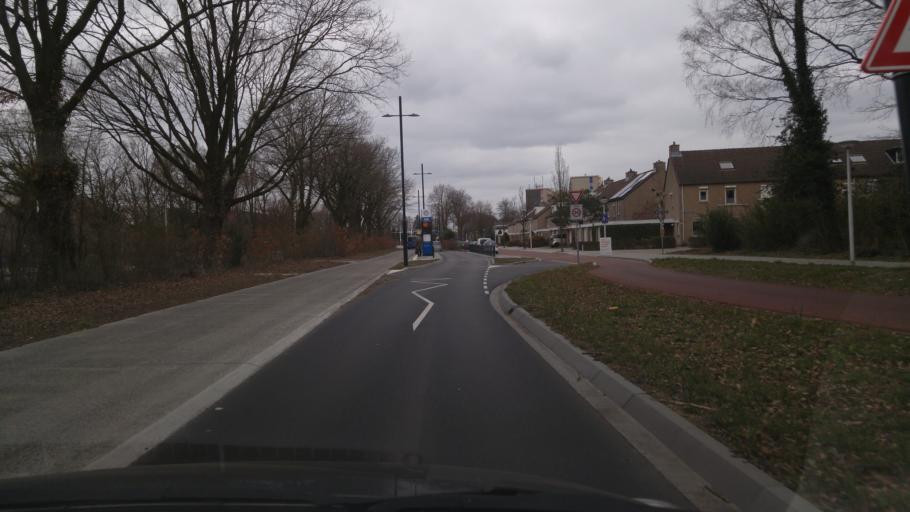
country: NL
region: North Brabant
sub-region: Gemeente Eindhoven
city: Eindhoven
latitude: 51.4768
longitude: 5.4585
